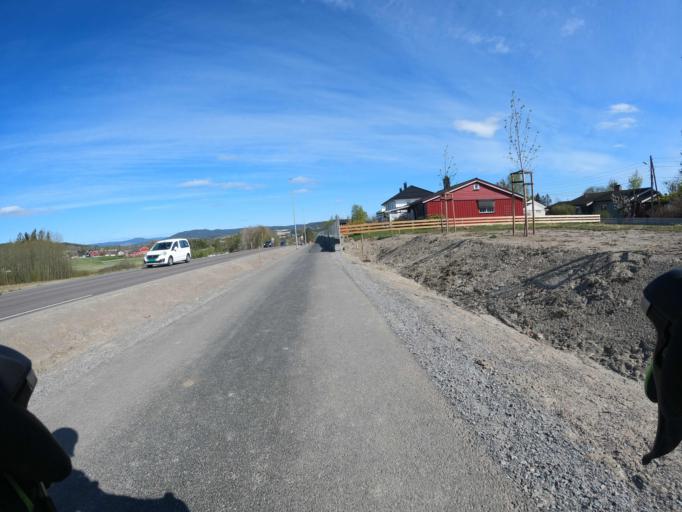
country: NO
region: Akershus
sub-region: Lorenskog
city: Kjenn
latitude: 59.9632
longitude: 10.9949
